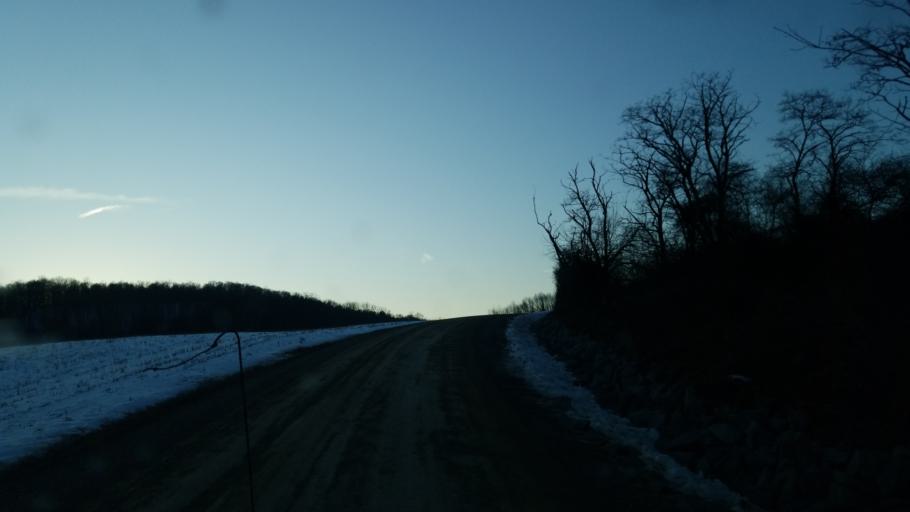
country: US
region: Pennsylvania
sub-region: Tioga County
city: Westfield
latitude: 42.0370
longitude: -77.5840
